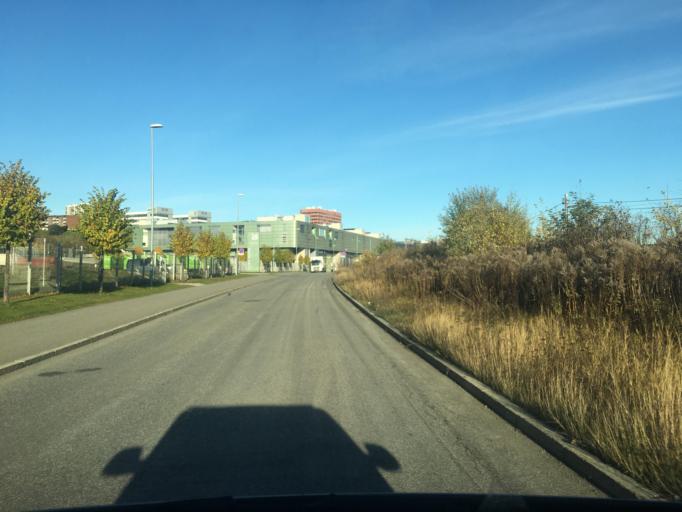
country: NO
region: Oslo
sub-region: Oslo
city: Oslo
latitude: 59.9354
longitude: 10.8373
